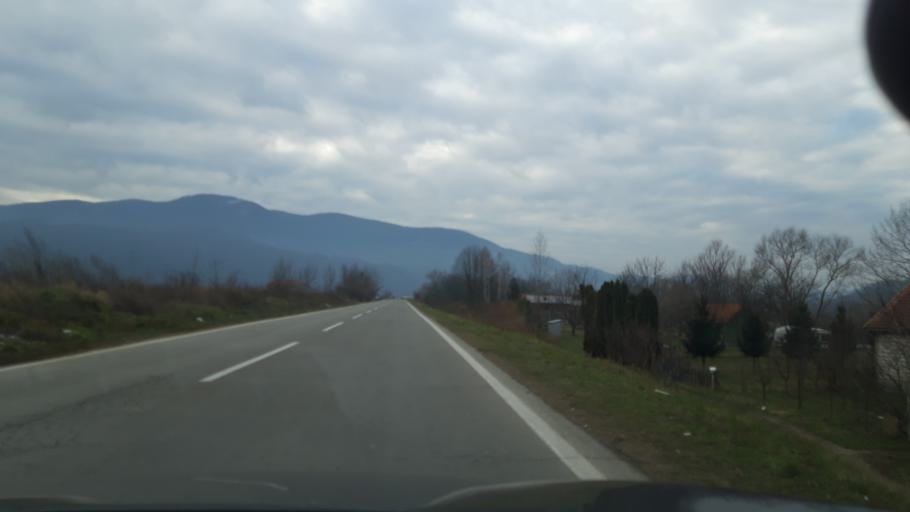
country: RS
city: Trsic
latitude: 44.5332
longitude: 19.1812
